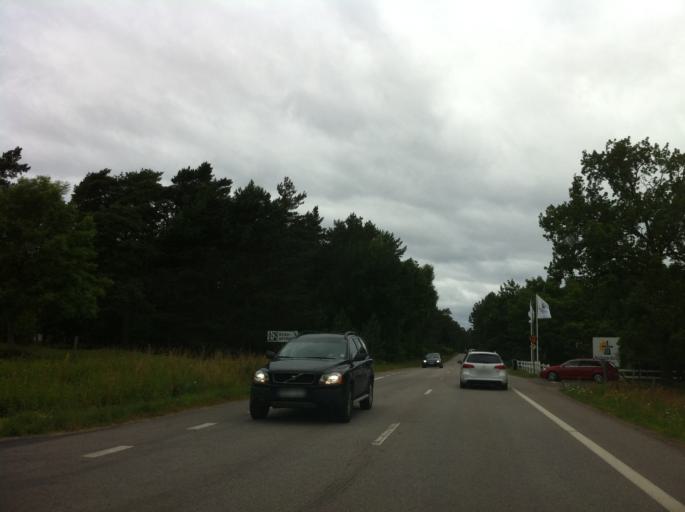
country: SE
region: Kalmar
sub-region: Borgholms Kommun
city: Borgholm
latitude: 57.2538
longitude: 17.0524
